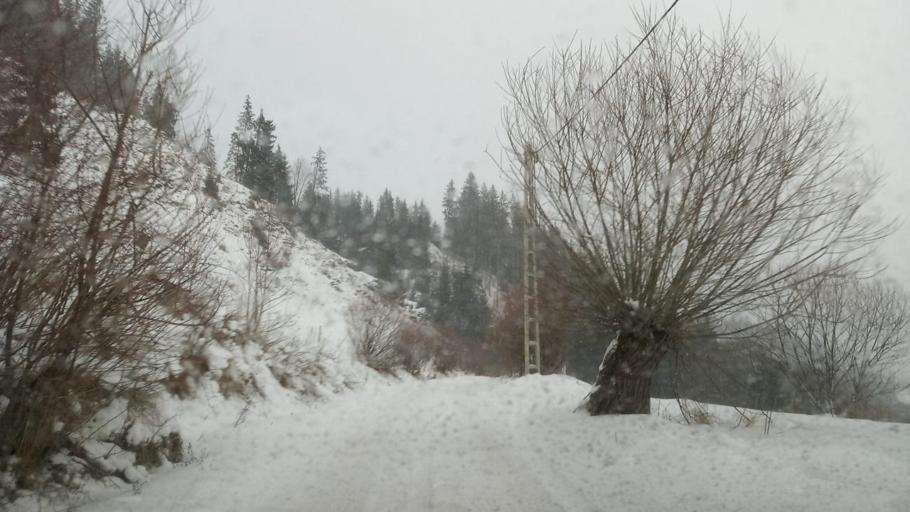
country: RO
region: Suceava
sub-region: Comuna Dorna Candrenilor
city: Dorna Candrenilor
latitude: 47.3578
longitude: 25.2952
